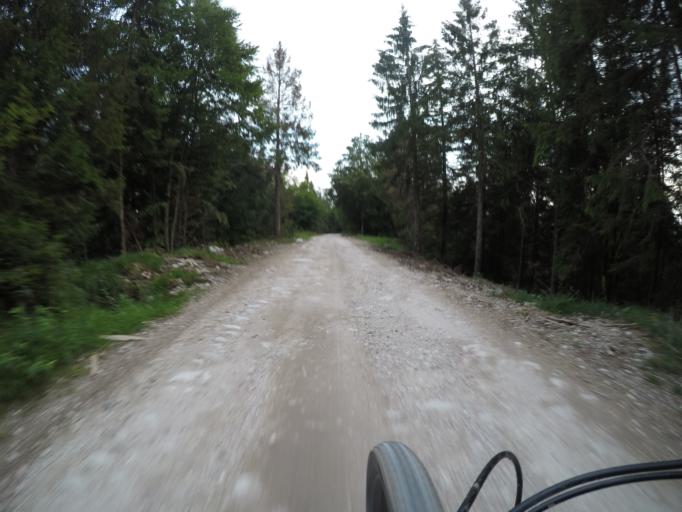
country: IT
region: Veneto
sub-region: Provincia di Vicenza
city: Gallio
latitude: 45.9031
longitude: 11.5256
